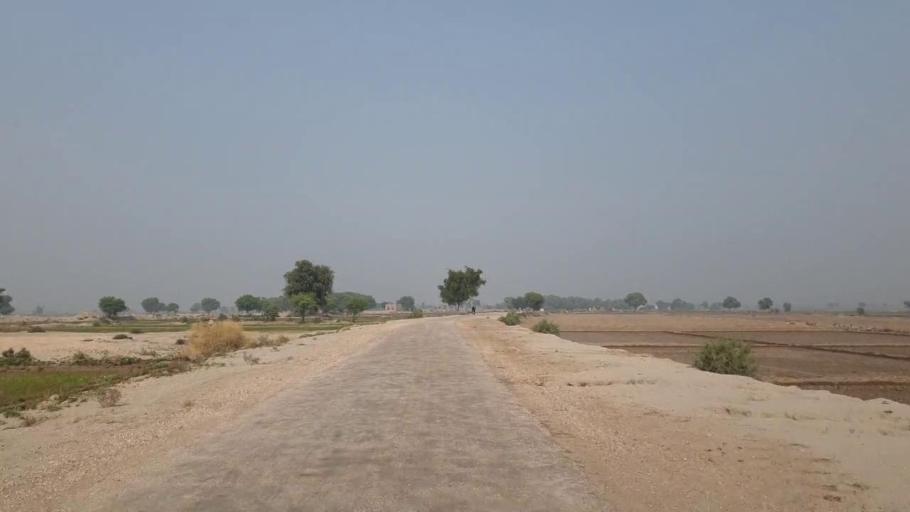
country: PK
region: Sindh
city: Bhan
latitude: 26.5180
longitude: 67.6898
